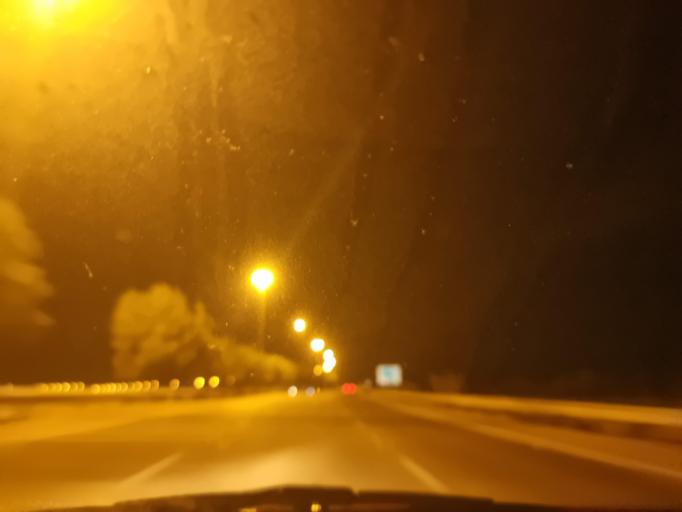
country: AE
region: Abu Dhabi
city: Abu Dhabi
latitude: 24.1830
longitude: 55.0330
